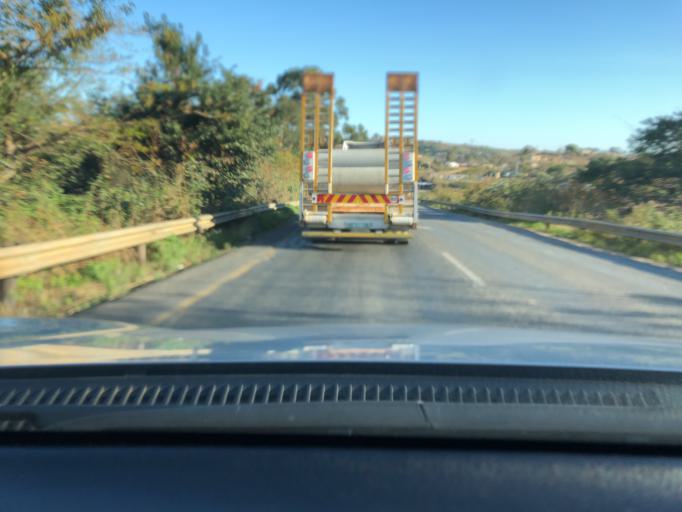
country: ZA
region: KwaZulu-Natal
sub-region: eThekwini Metropolitan Municipality
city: Umkomaas
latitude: -30.0339
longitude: 30.8101
